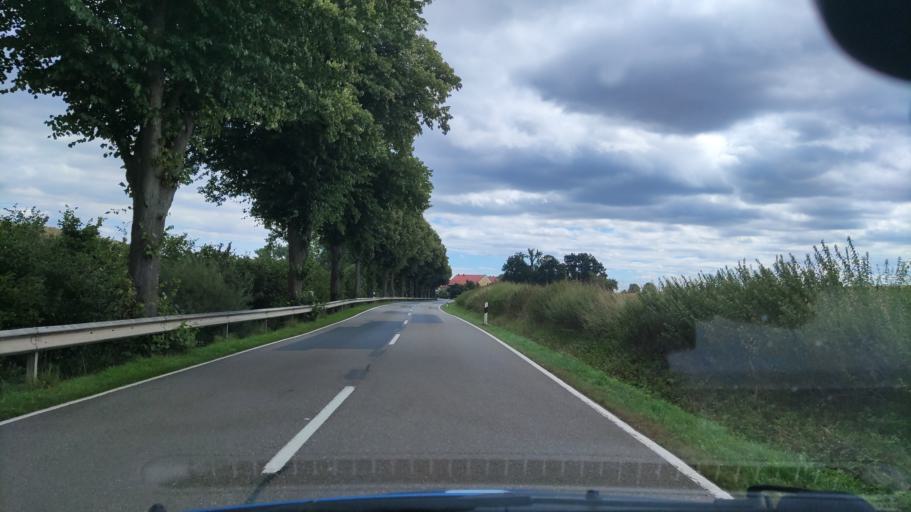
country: DE
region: Lower Saxony
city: Eimen
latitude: 51.8282
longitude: 9.8084
